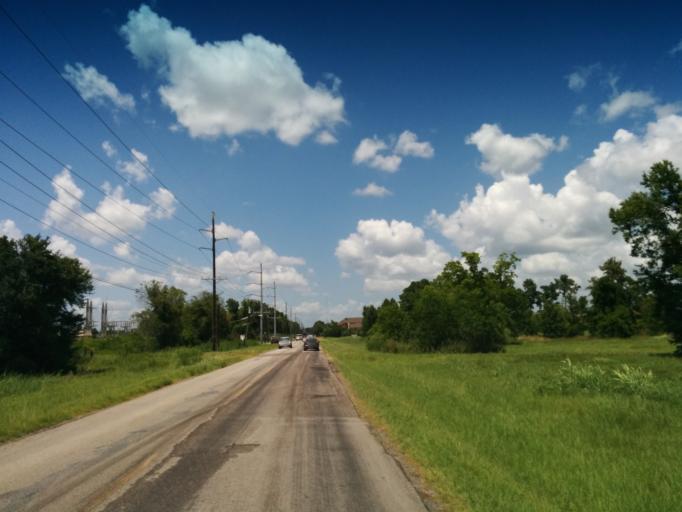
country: US
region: Texas
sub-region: Jefferson County
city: Beaumont
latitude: 30.1241
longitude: -94.1689
